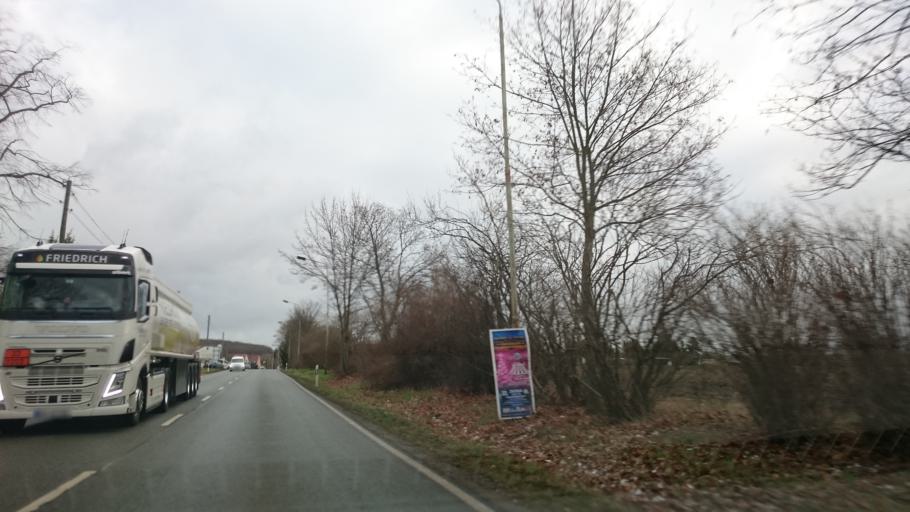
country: DE
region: Saxony
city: Werdau
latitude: 50.7347
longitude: 12.3915
